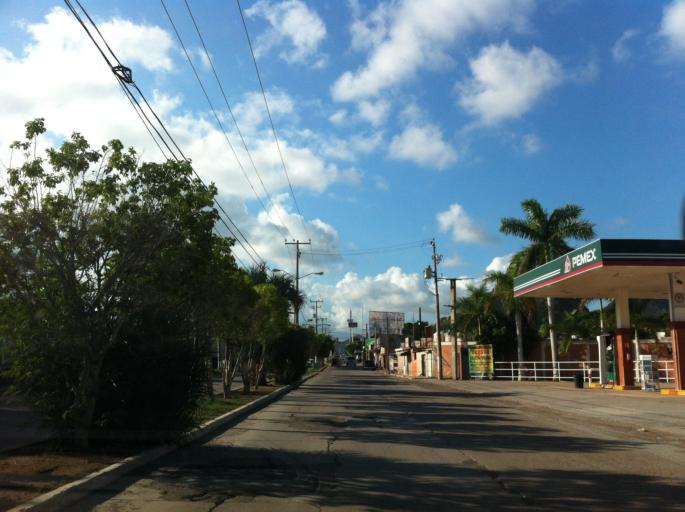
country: MX
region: Sonora
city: Heroica Guaymas
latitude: 27.9219
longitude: -110.9171
